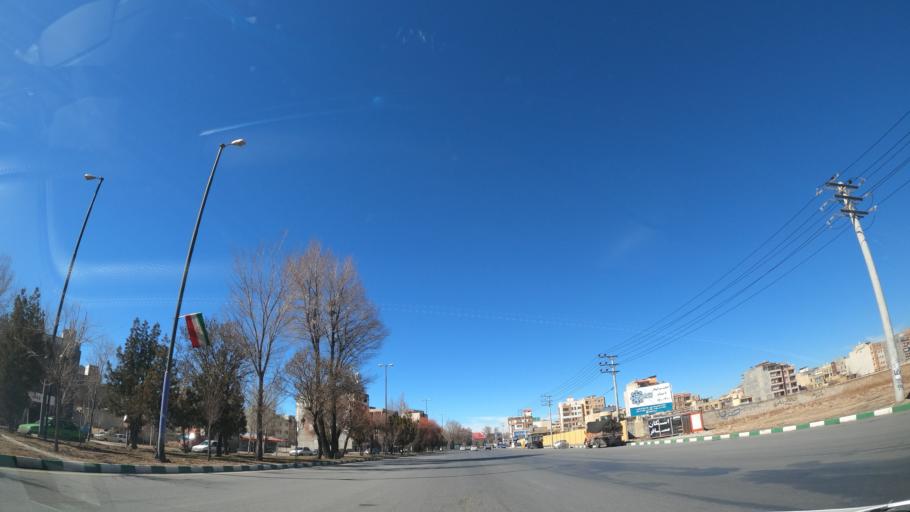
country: IR
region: Chahar Mahall va Bakhtiari
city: Shahrekord
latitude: 32.3103
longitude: 50.8910
